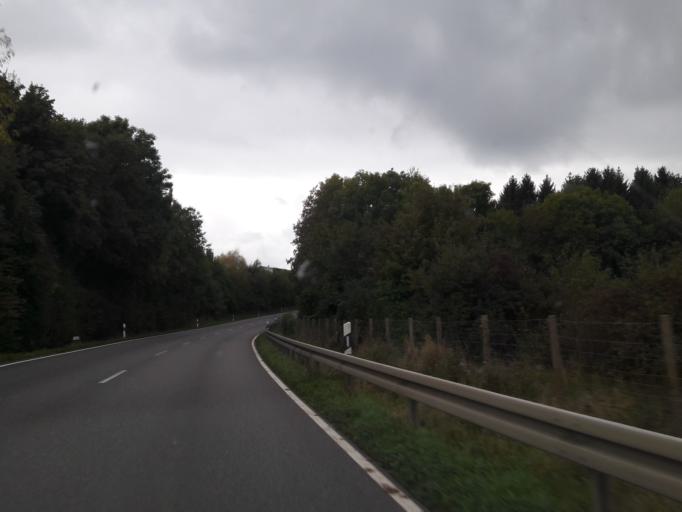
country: DE
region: Baden-Wuerttemberg
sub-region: Regierungsbezirk Stuttgart
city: Mockmuhl
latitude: 49.2916
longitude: 9.3670
